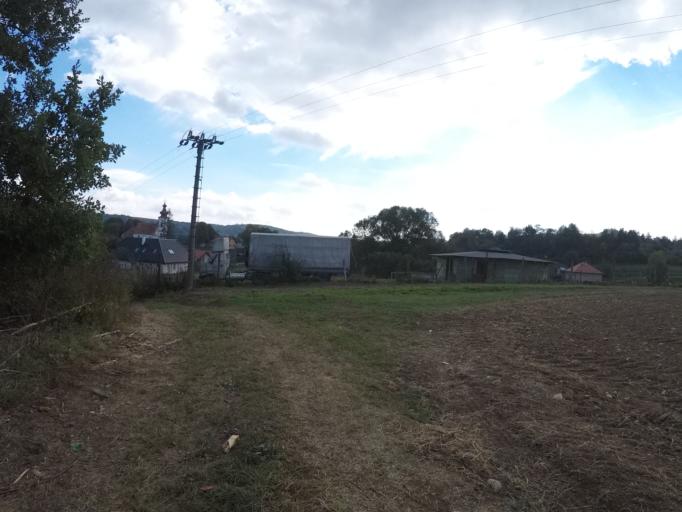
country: SK
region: Presovsky
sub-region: Okres Presov
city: Presov
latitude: 48.9292
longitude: 21.1844
